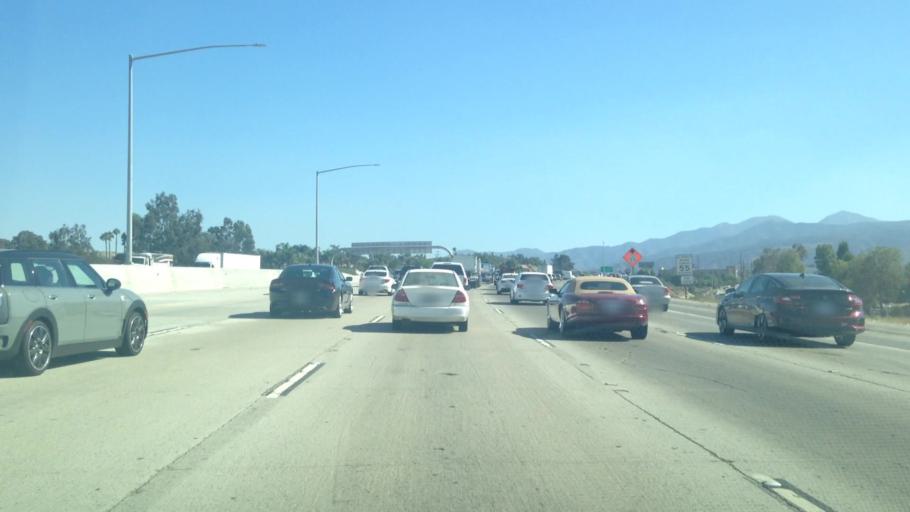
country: US
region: California
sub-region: Riverside County
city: El Cerrito
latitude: 33.8581
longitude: -117.5383
